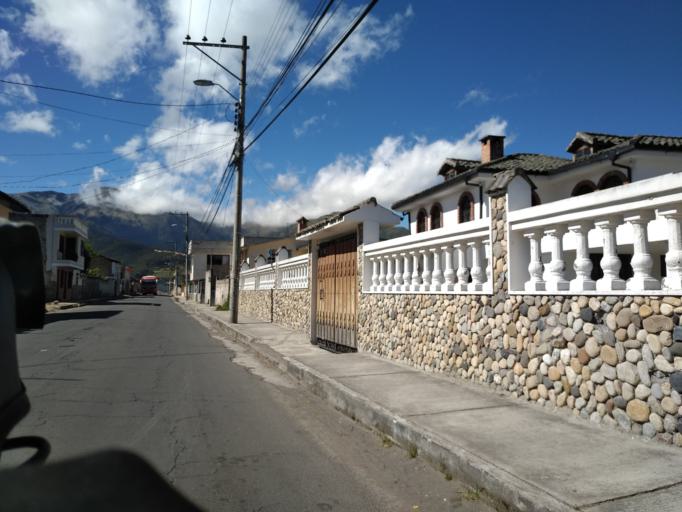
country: EC
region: Imbabura
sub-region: Canton Otavalo
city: Otavalo
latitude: 0.2020
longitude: -78.1957
